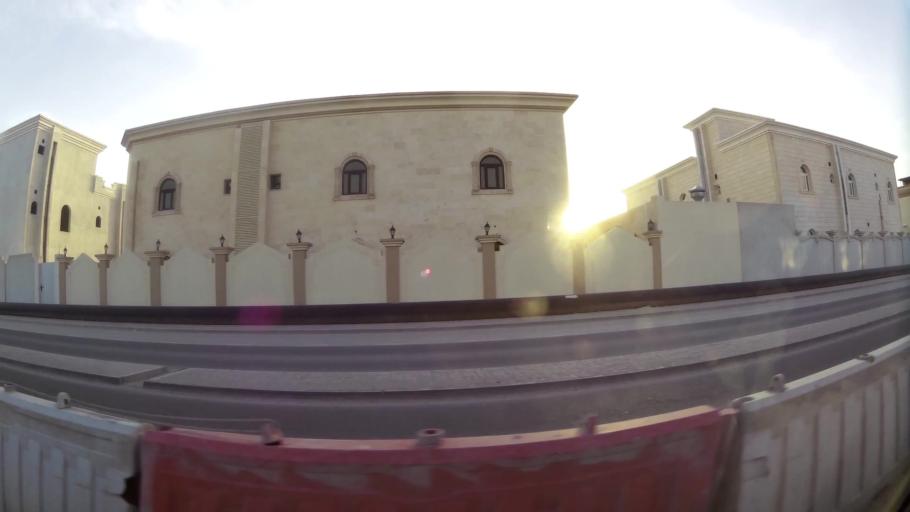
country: QA
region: Al Wakrah
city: Al Wakrah
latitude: 25.1591
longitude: 51.5915
